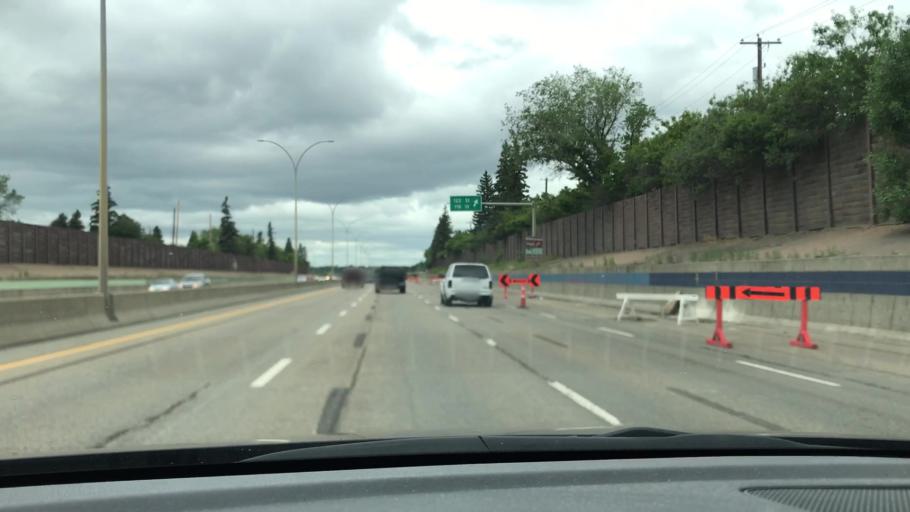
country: CA
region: Alberta
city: Edmonton
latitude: 53.4832
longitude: -113.5318
